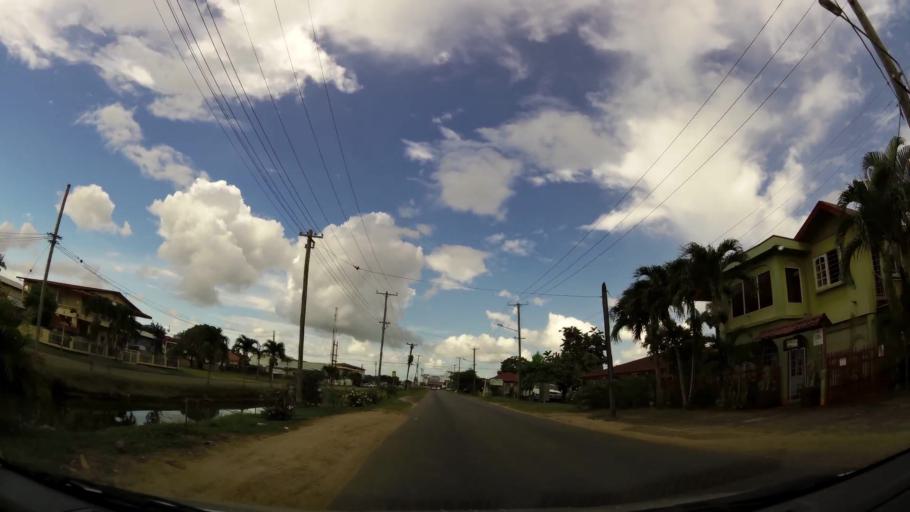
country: SR
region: Paramaribo
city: Paramaribo
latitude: 5.8498
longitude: -55.1342
